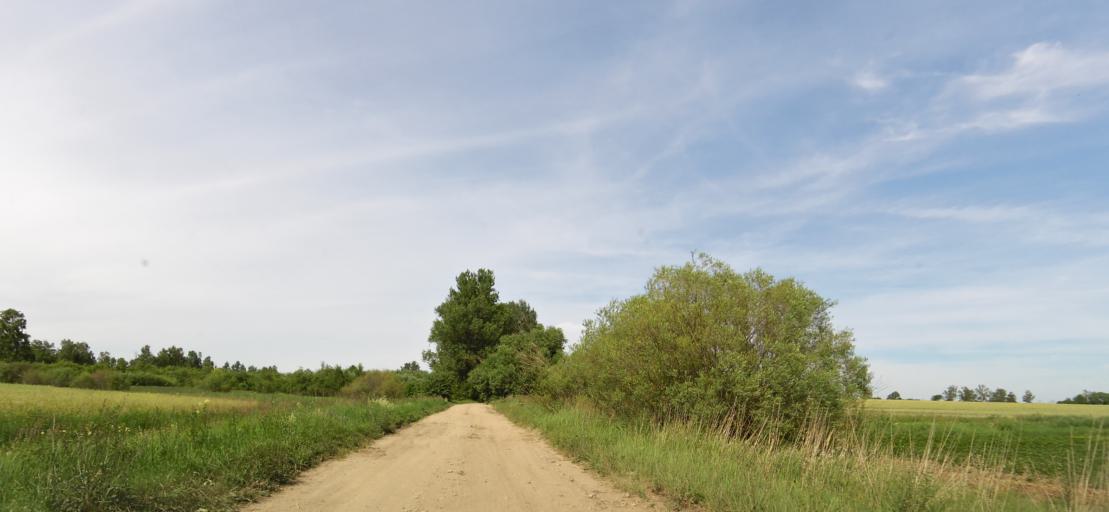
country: LT
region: Panevezys
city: Pasvalys
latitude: 55.9137
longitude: 24.2924
